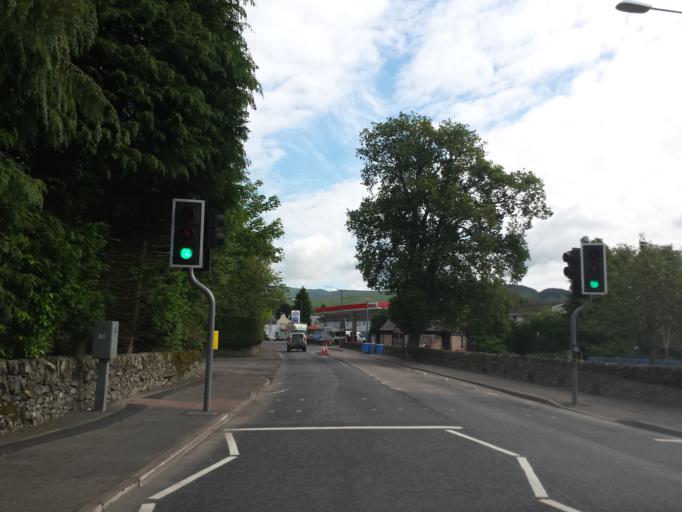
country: GB
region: Scotland
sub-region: Dumfries and Galloway
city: Moffat
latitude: 55.3300
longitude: -3.4451
